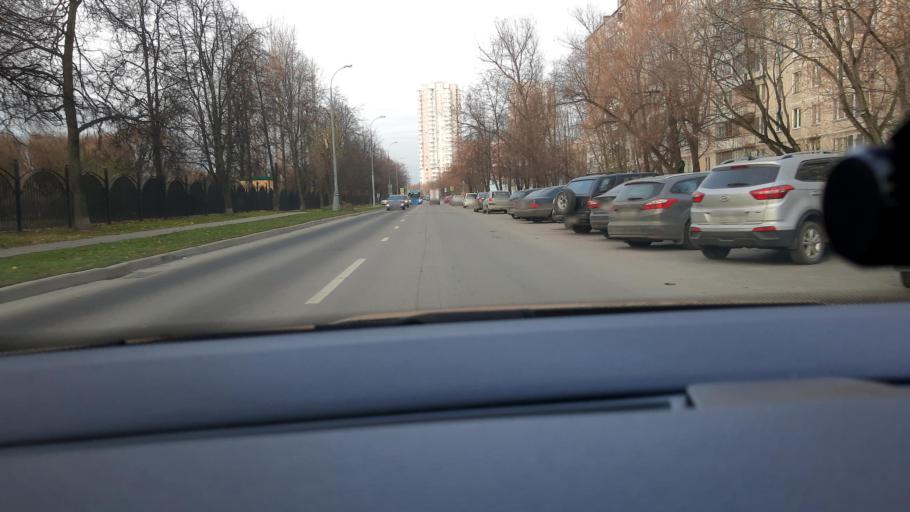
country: RU
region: Moscow
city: Tekstil'shchiki
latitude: 55.6833
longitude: 37.7173
